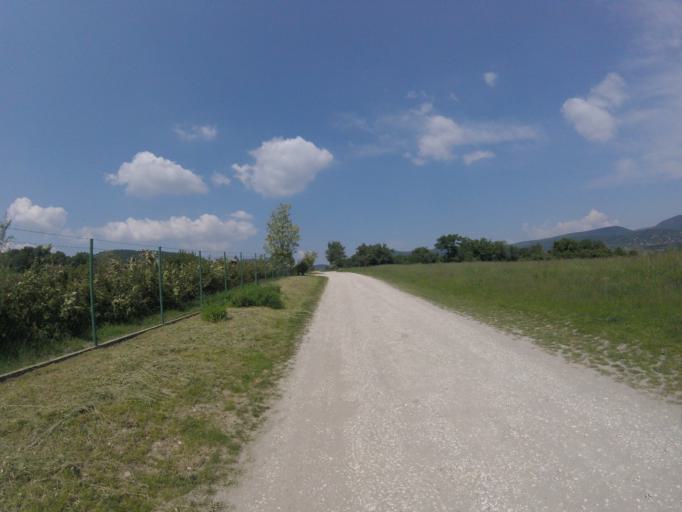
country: HU
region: Pest
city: Nagykovacsi
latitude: 47.6798
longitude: 19.0381
